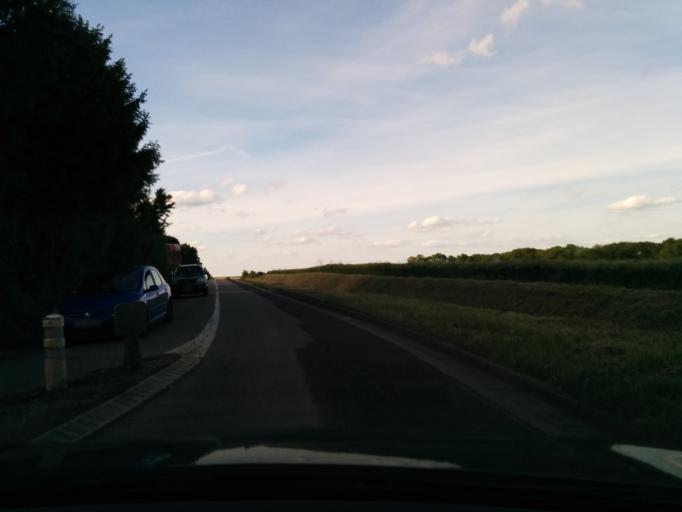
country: FR
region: Haute-Normandie
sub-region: Departement de l'Eure
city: Les Andelys
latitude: 49.2808
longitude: 1.4117
